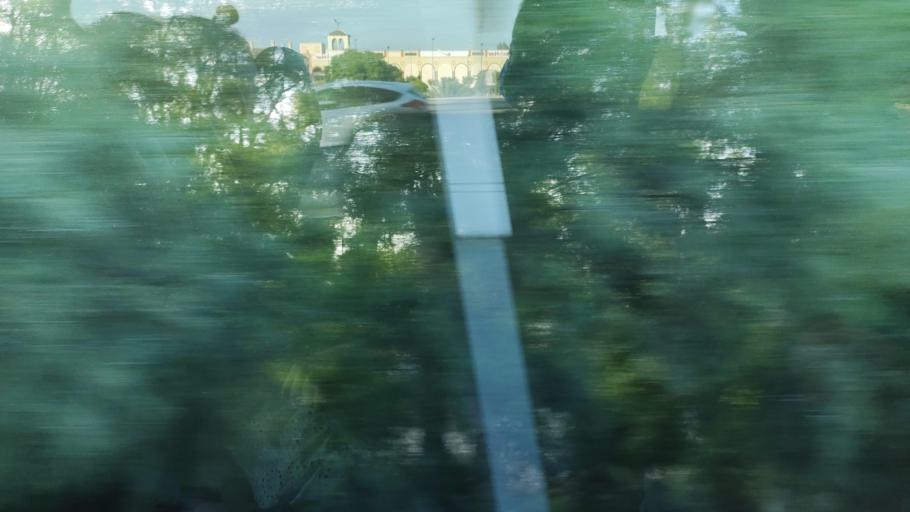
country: ES
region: Andalusia
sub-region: Provincia de Malaga
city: Torremolinos
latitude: 36.6543
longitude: -4.4775
